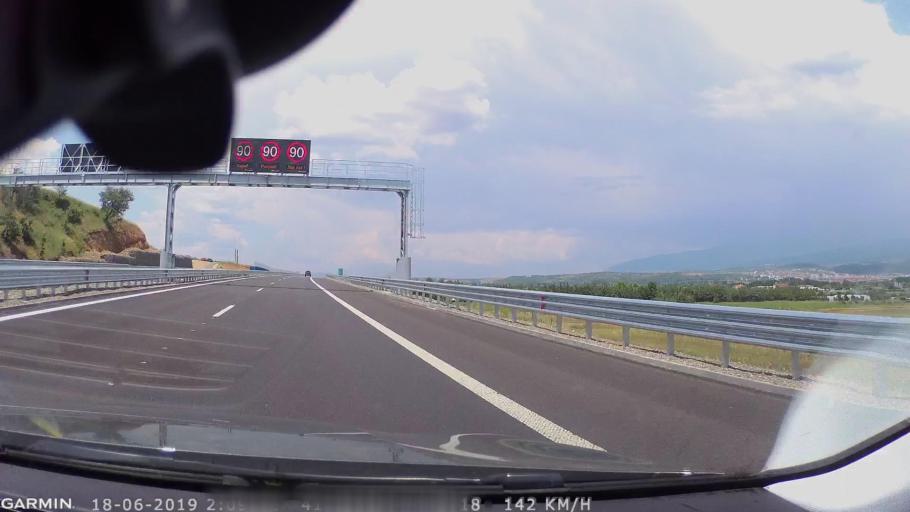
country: BG
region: Blagoevgrad
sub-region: Obshtina Blagoevgrad
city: Blagoevgrad
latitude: 41.9783
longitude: 23.0666
